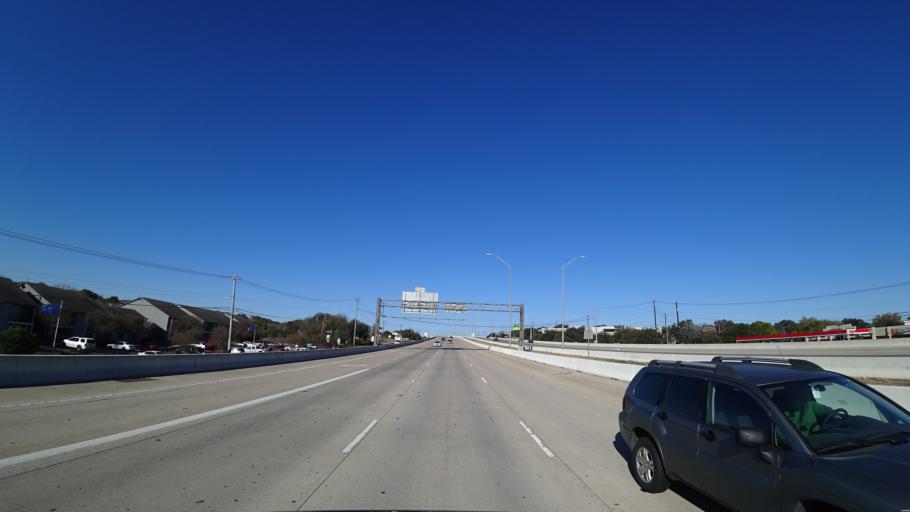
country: US
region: Texas
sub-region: Travis County
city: Austin
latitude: 30.3295
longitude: -97.6799
